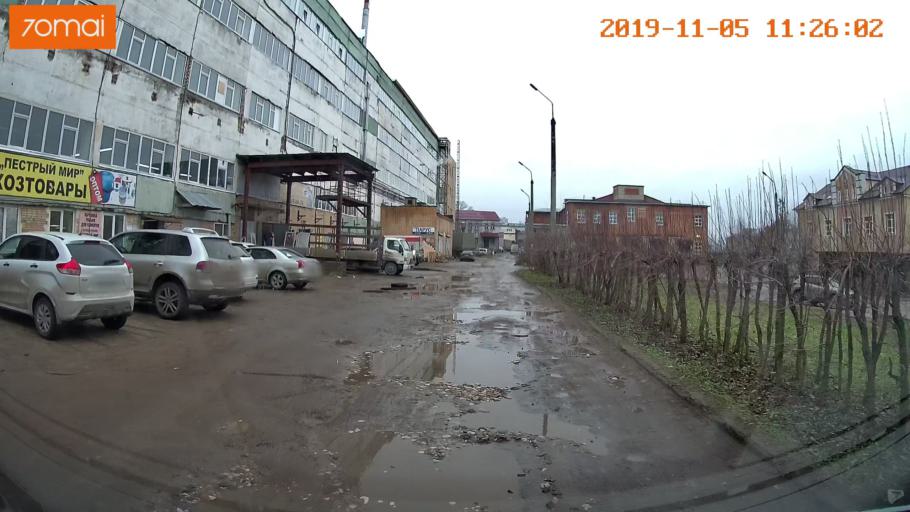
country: RU
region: Ivanovo
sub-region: Gorod Ivanovo
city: Ivanovo
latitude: 57.0108
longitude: 40.9582
